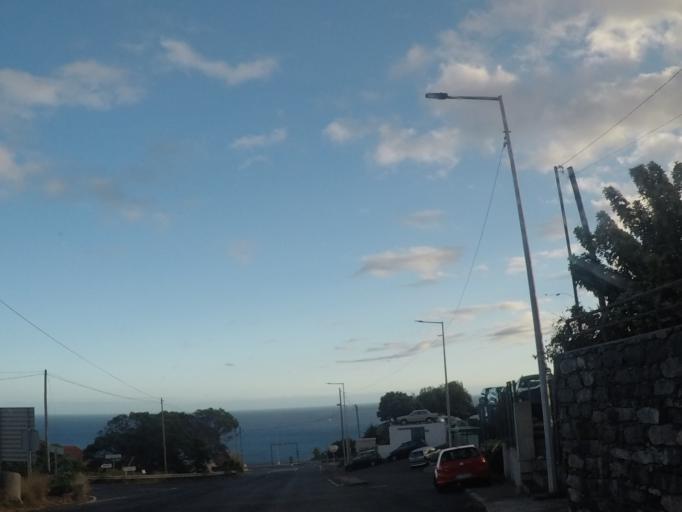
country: PT
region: Madeira
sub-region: Santa Cruz
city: Santa Cruz
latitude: 32.6592
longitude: -16.8125
